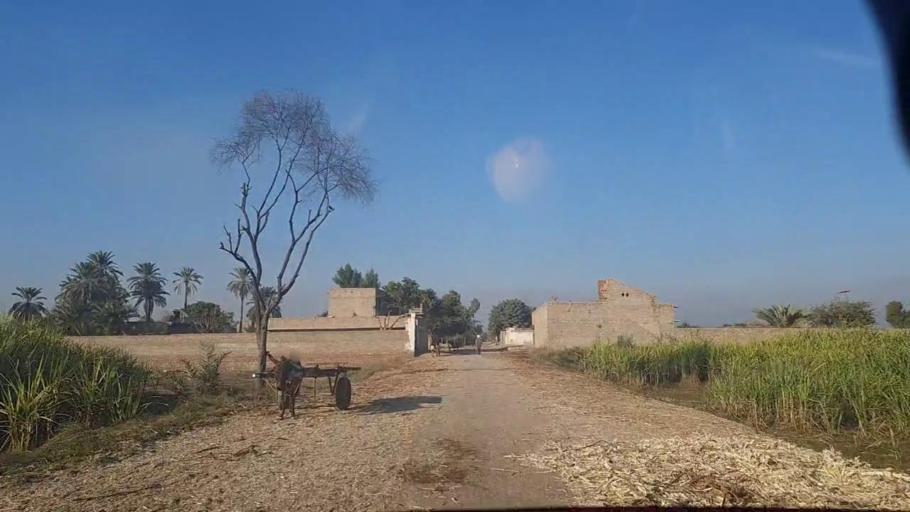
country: PK
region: Sindh
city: Sobhadero
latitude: 27.4168
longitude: 68.4230
